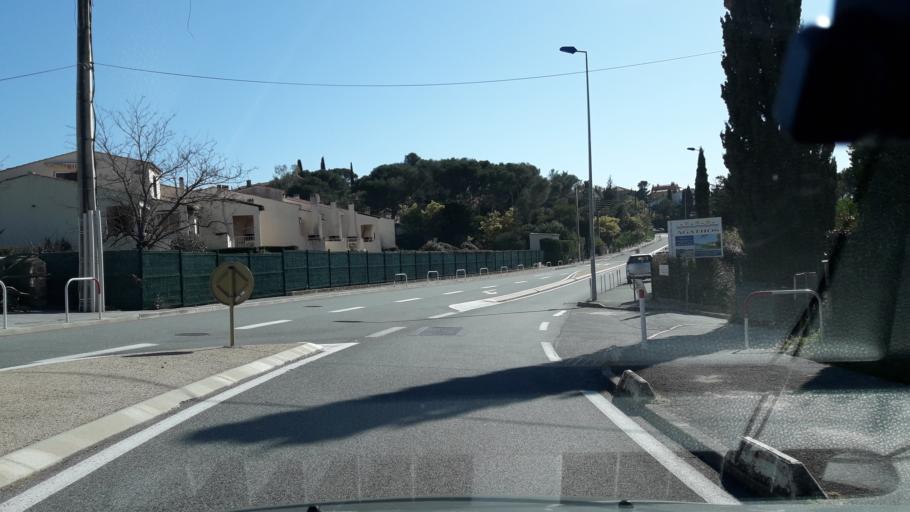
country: FR
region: Provence-Alpes-Cote d'Azur
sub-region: Departement du Var
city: Saint-Raphael
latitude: 43.4304
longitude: 6.8709
